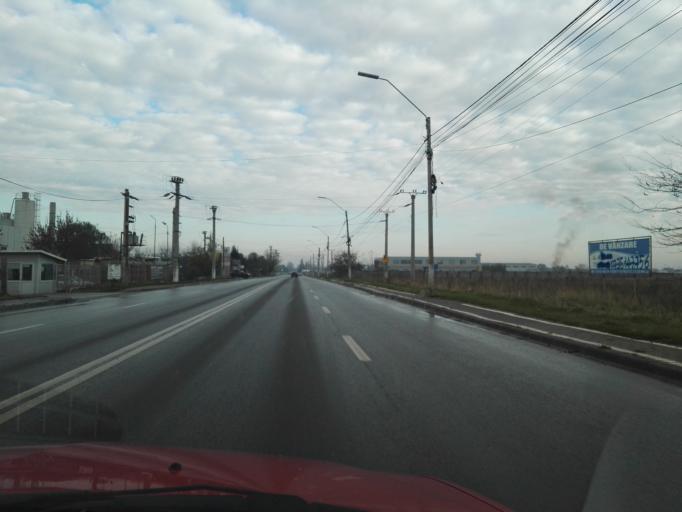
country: RO
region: Ilfov
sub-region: Comuna Magurele
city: Magurele
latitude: 44.3686
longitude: 26.0421
